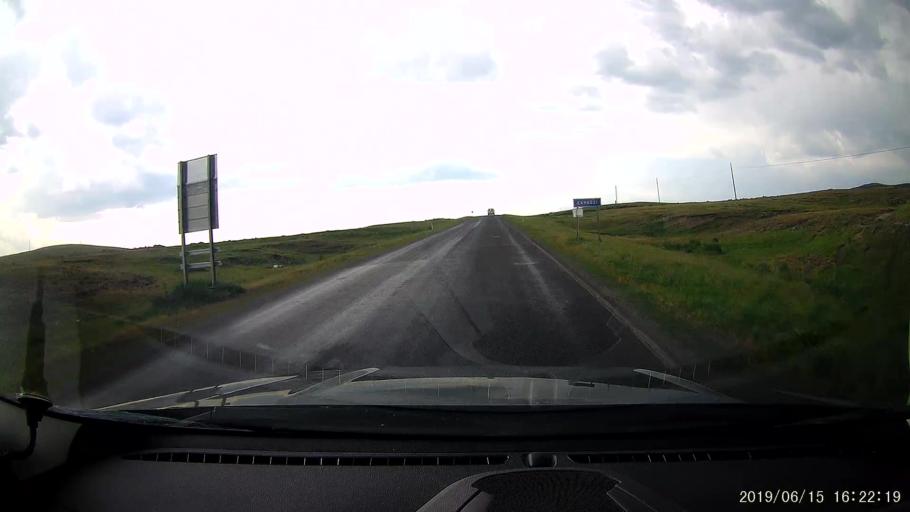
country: TR
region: Ardahan
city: Hanak
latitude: 41.1892
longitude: 42.8493
